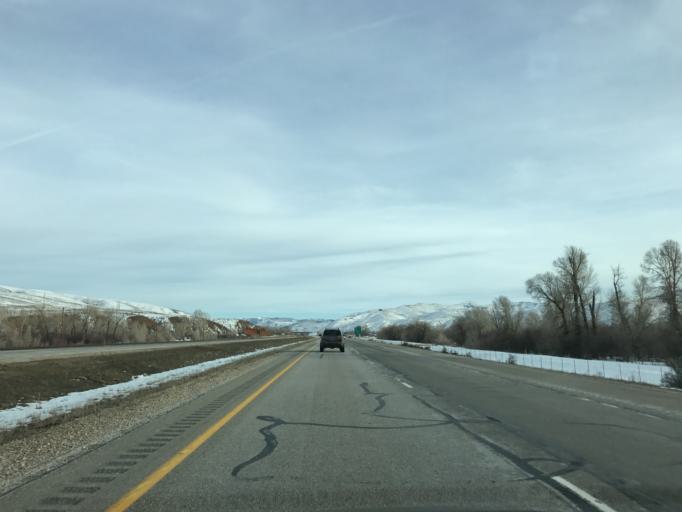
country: US
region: Utah
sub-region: Summit County
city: Coalville
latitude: 41.0267
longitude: -111.4987
